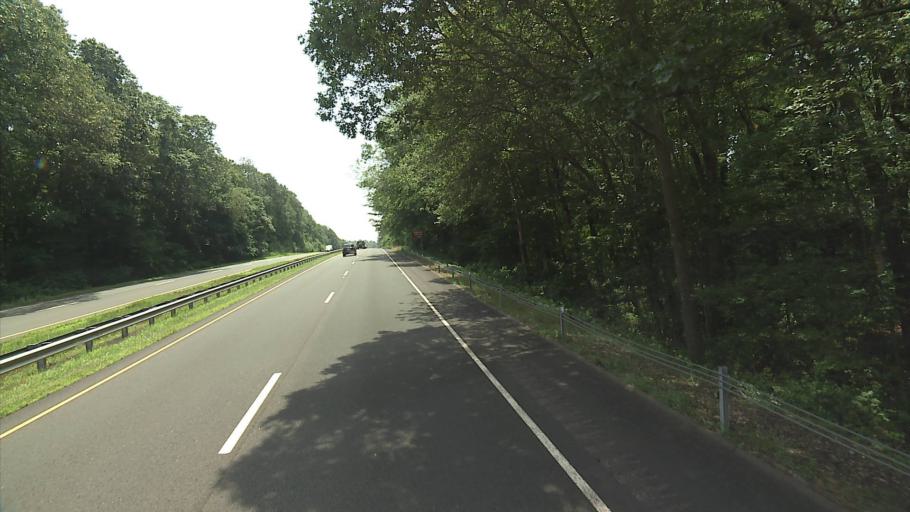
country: US
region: Connecticut
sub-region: New Haven County
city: Madison
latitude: 41.2791
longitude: -72.5641
